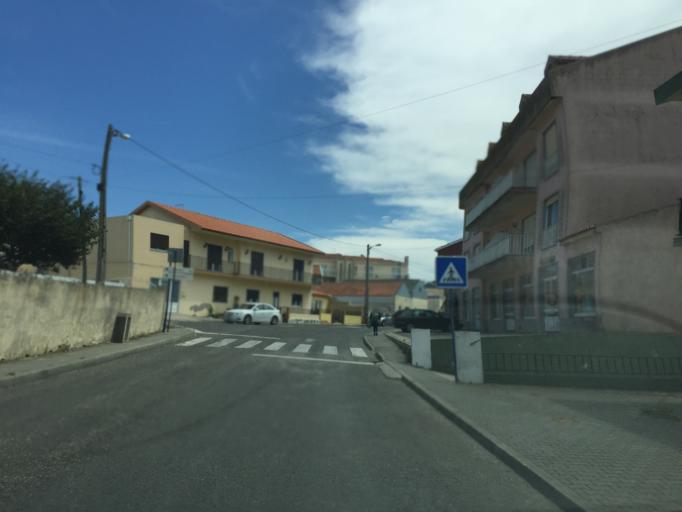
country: PT
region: Lisbon
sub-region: Lourinha
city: Lourinha
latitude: 39.2011
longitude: -9.3329
